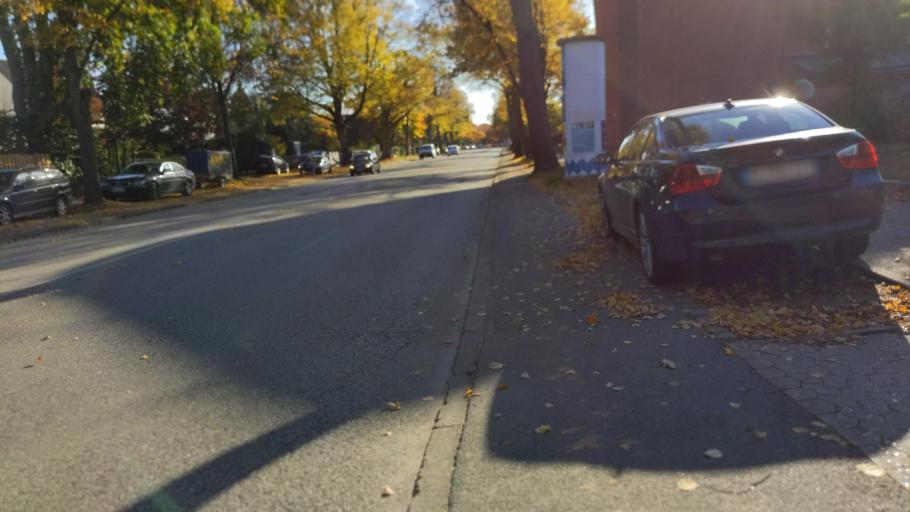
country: DE
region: Schleswig-Holstein
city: Luebeck
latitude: 53.8657
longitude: 10.7119
